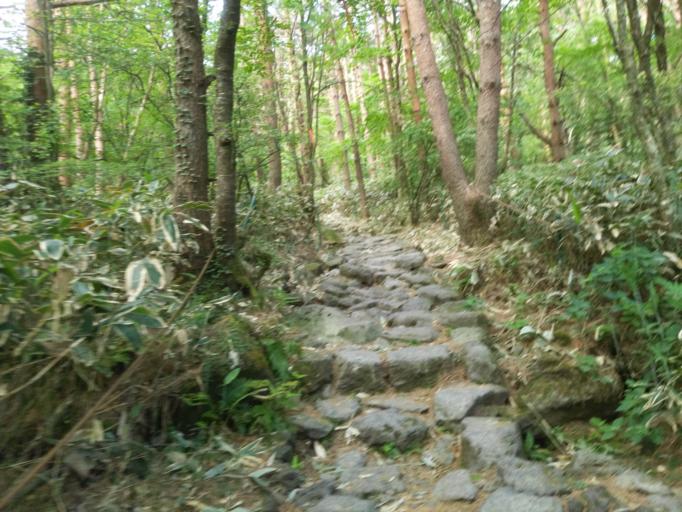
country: KR
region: Jeju-do
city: Jeju-si
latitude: 33.3888
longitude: 126.5376
